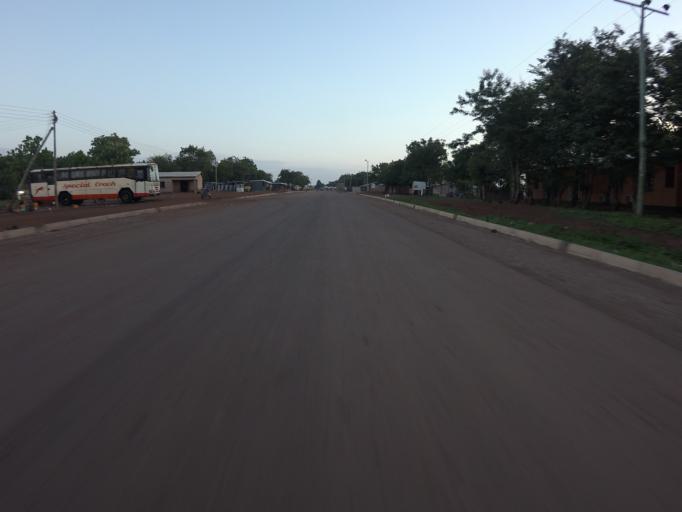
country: GH
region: Northern
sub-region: Yendi
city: Yendi
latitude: 9.9252
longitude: -0.2127
